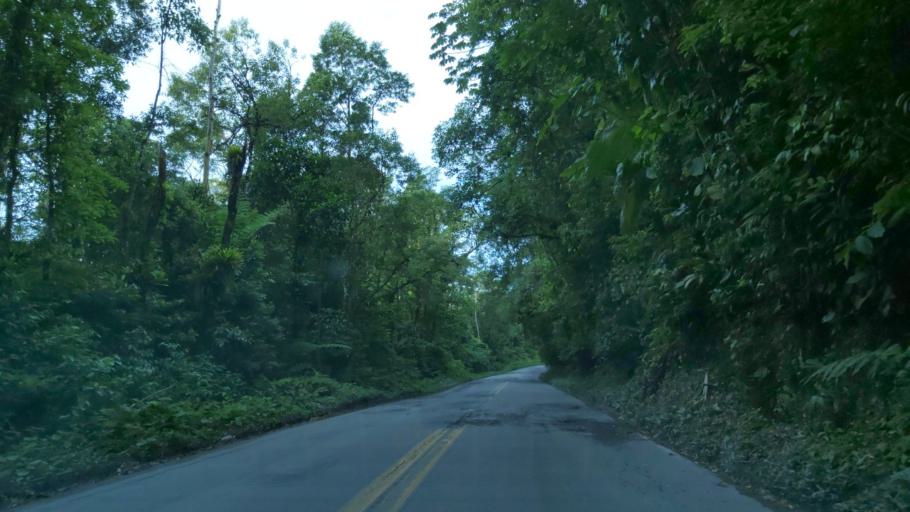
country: BR
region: Sao Paulo
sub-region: Miracatu
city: Miracatu
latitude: -24.0372
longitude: -47.5669
